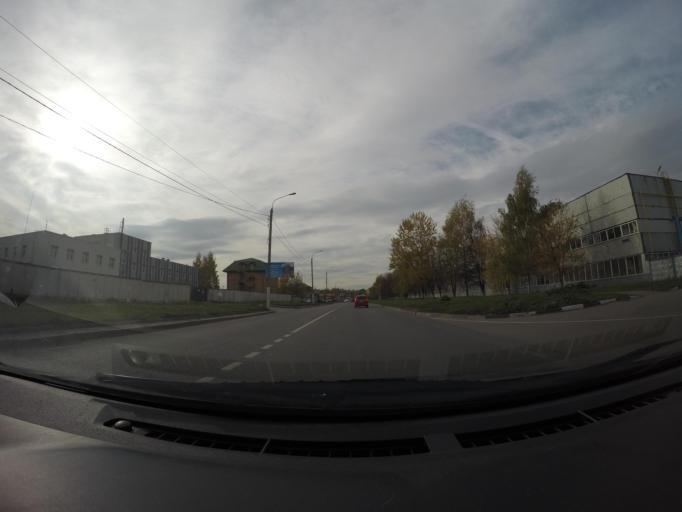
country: RU
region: Moskovskaya
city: Dolgoprudnyy
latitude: 55.9200
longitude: 37.5031
